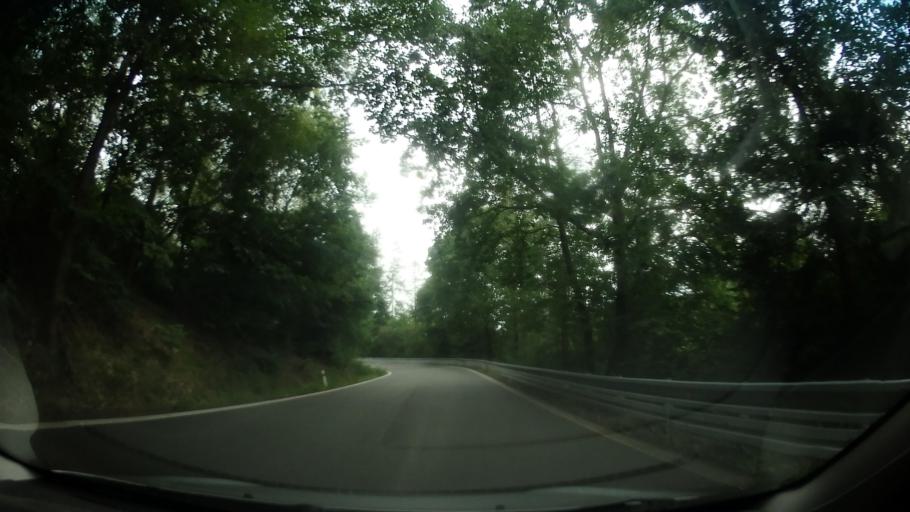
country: CZ
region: Central Bohemia
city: Bystrice
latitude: 49.7588
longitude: 14.6235
